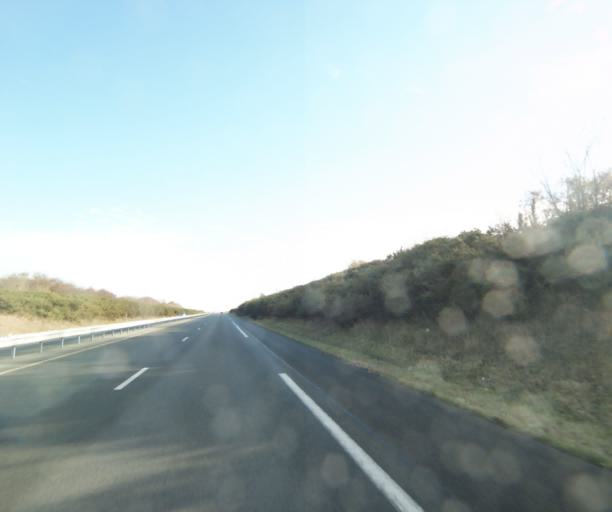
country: FR
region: Poitou-Charentes
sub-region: Departement de la Charente-Maritime
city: Saint-Romain-de-Benet
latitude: 45.6958
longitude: -0.8170
